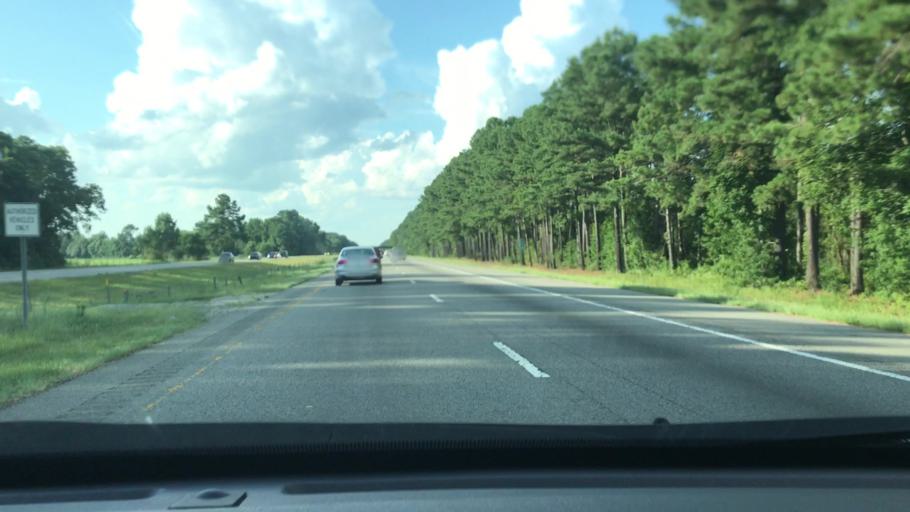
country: US
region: North Carolina
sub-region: Robeson County
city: Saint Pauls
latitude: 34.7628
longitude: -78.9967
